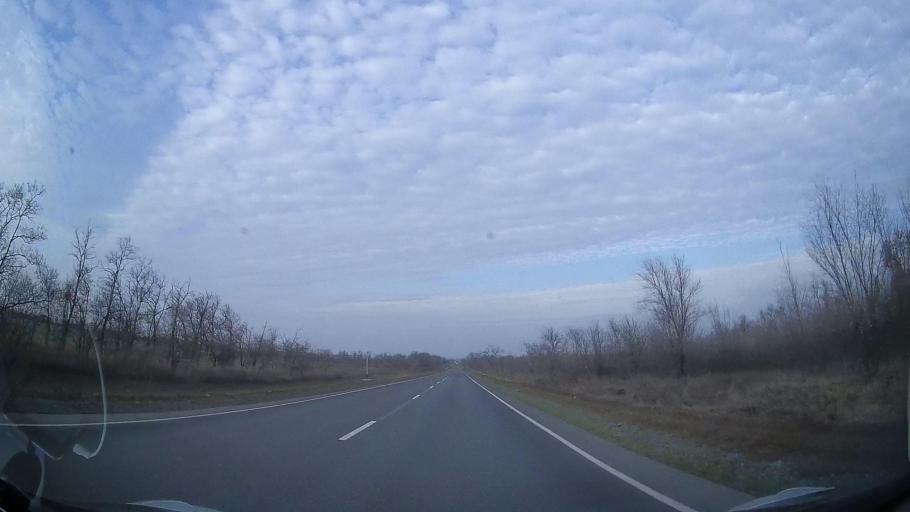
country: RU
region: Rostov
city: Bagayevskaya
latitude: 47.1492
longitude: 40.2765
